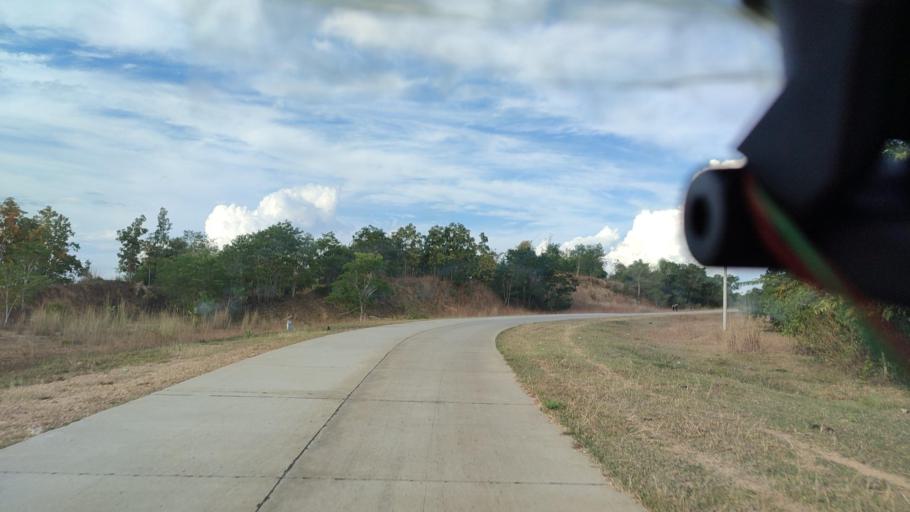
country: MM
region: Mandalay
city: Yamethin
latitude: 20.0998
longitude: 96.0352
